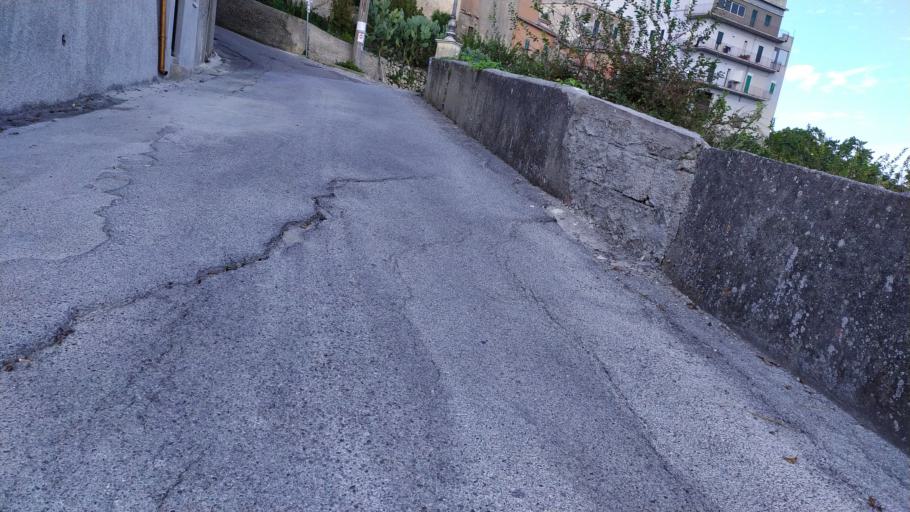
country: IT
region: Sicily
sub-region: Messina
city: Rometta
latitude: 38.1704
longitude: 15.4155
